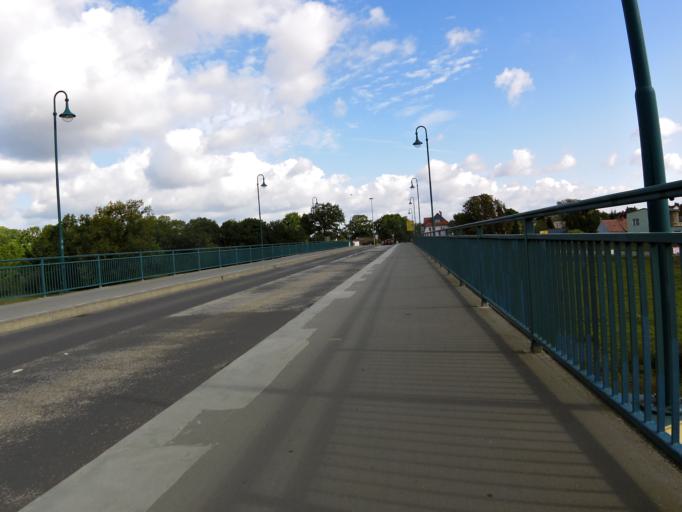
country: DE
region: Saxony-Anhalt
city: Schonebeck
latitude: 52.0277
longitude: 11.7415
